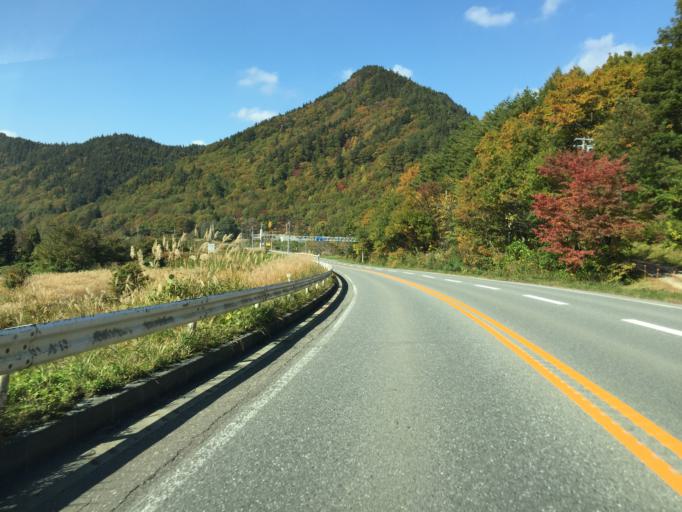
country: JP
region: Yamagata
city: Yonezawa
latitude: 37.8665
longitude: 140.2309
